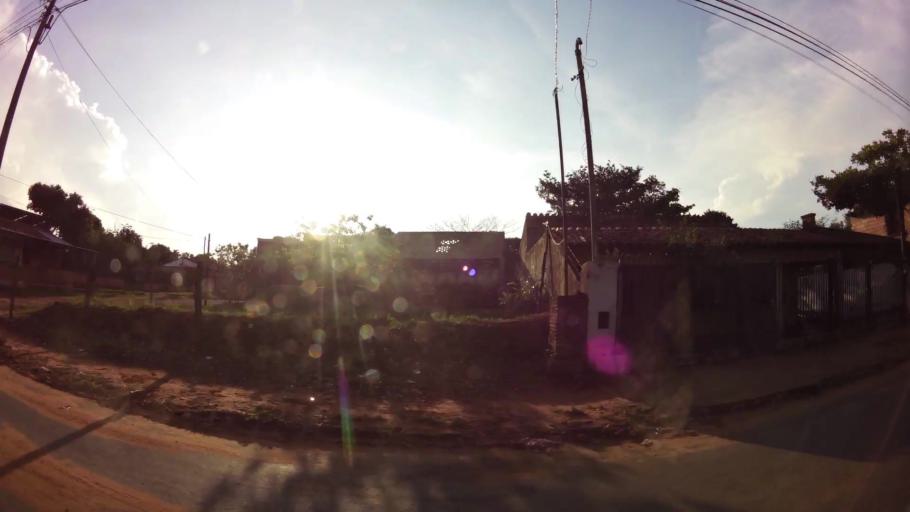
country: PY
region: Central
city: Fernando de la Mora
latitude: -25.3593
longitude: -57.5292
